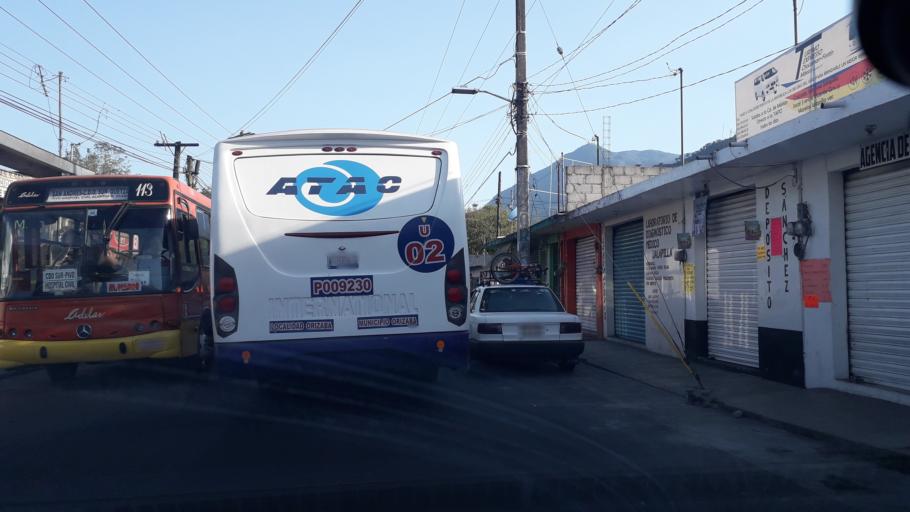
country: MX
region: Veracruz
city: Jalapilla
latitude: 18.8287
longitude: -97.0903
